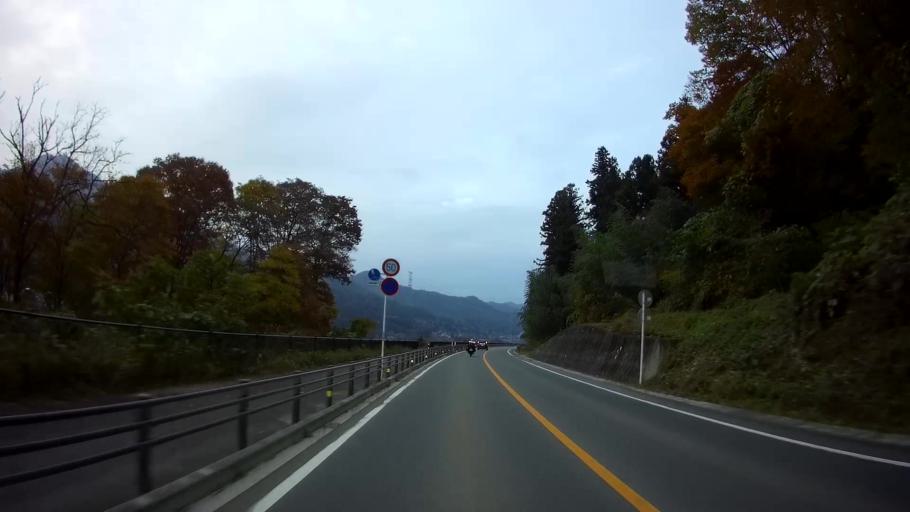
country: JP
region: Gunma
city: Nakanojomachi
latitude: 36.5664
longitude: 138.7388
